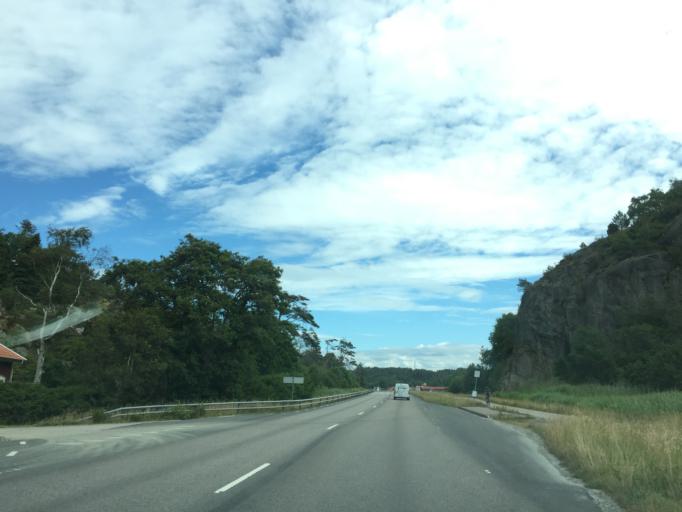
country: SE
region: Vaestra Goetaland
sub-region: Tjorns Kommun
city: Skaerhamn
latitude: 58.0234
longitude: 11.6437
